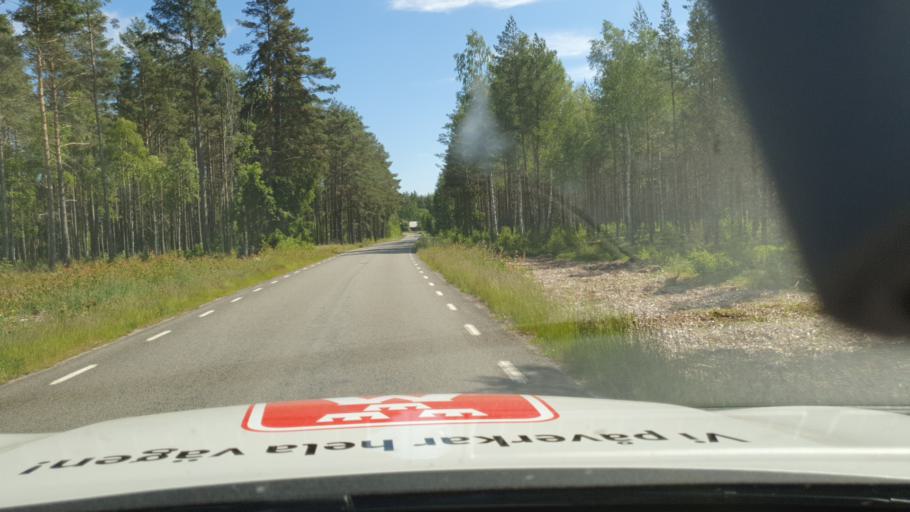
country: SE
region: Vaestra Goetaland
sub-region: Tidaholms Kommun
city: Olofstorp
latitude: 58.2760
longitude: 13.9656
